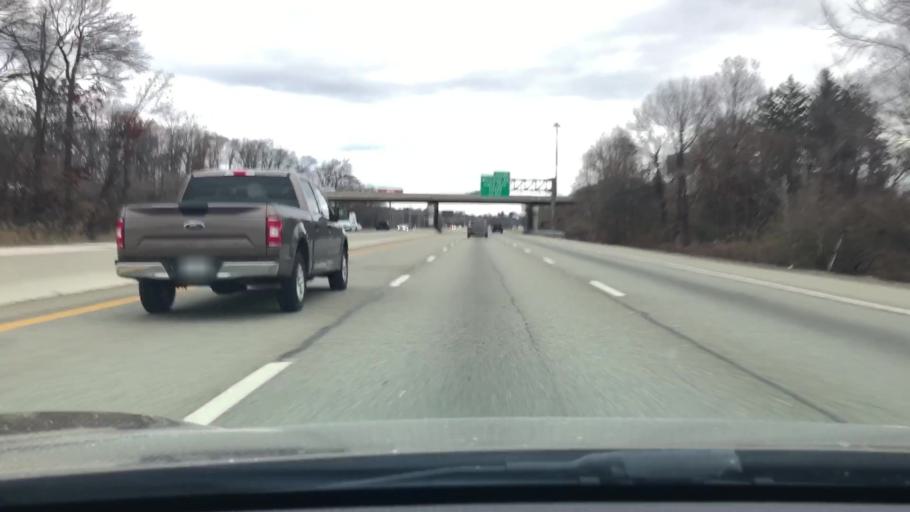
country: US
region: New Jersey
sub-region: Passaic County
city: Singac
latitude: 40.8969
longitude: -74.2518
